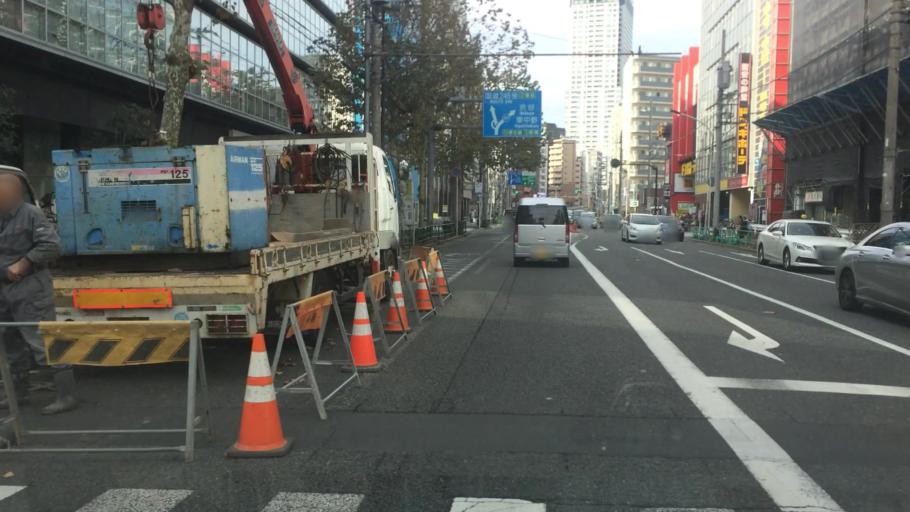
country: JP
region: Tokyo
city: Tokyo
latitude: 35.6479
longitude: 139.6937
